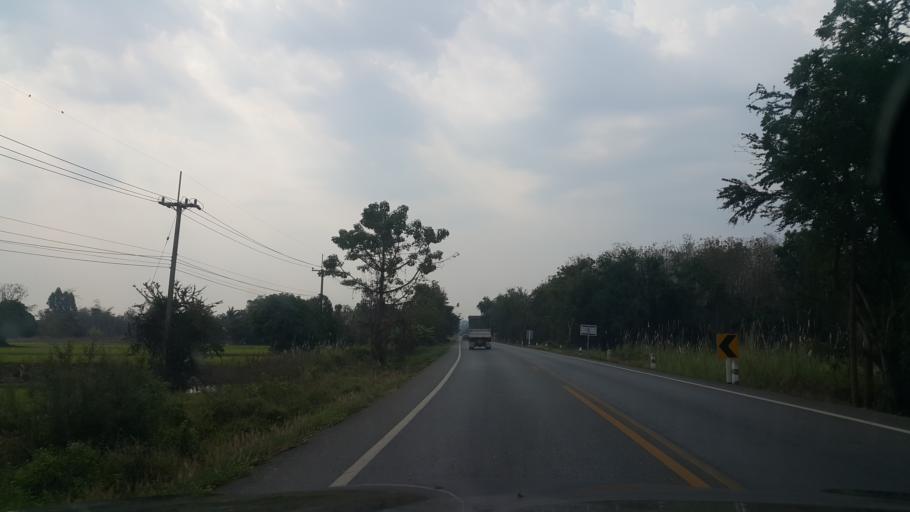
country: TH
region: Sukhothai
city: Si Samrong
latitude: 17.1125
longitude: 99.8894
